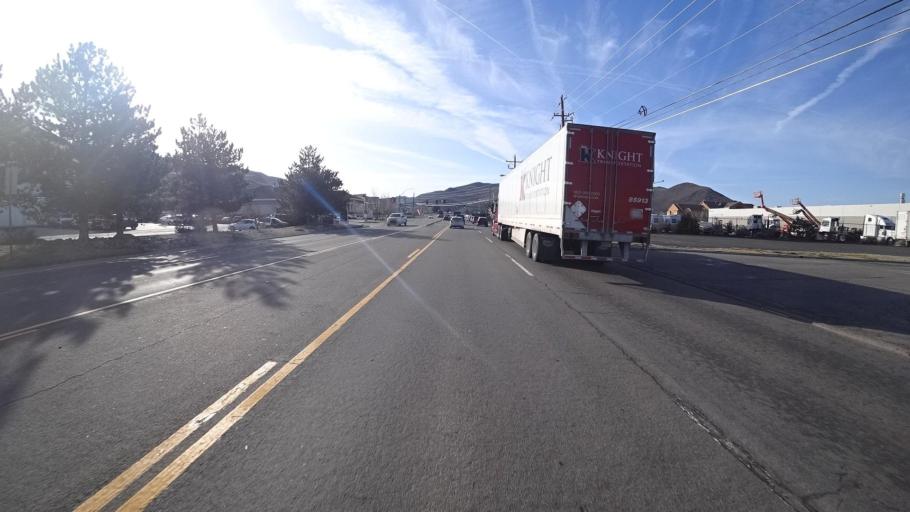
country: US
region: Nevada
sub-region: Washoe County
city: Sparks
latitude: 39.5297
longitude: -119.7022
